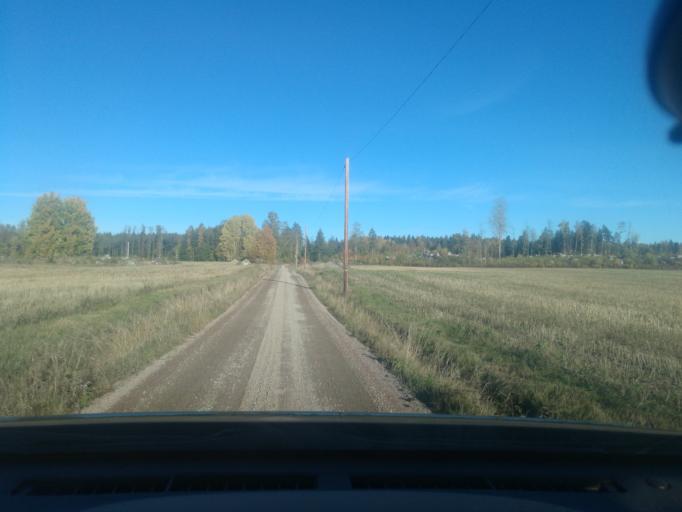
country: SE
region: Vaestmanland
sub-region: Kopings Kommun
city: Koping
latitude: 59.5954
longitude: 16.0188
